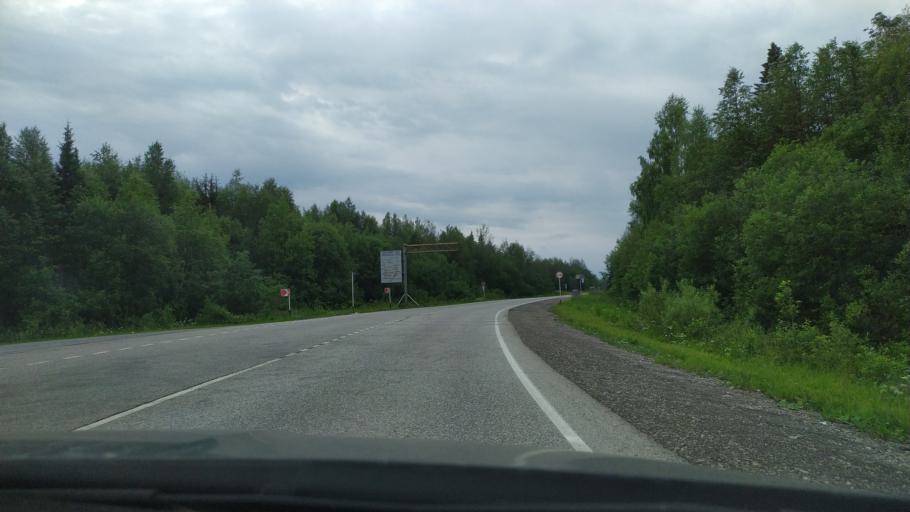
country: RU
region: Perm
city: Chusovoy
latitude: 58.3876
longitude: 57.9012
